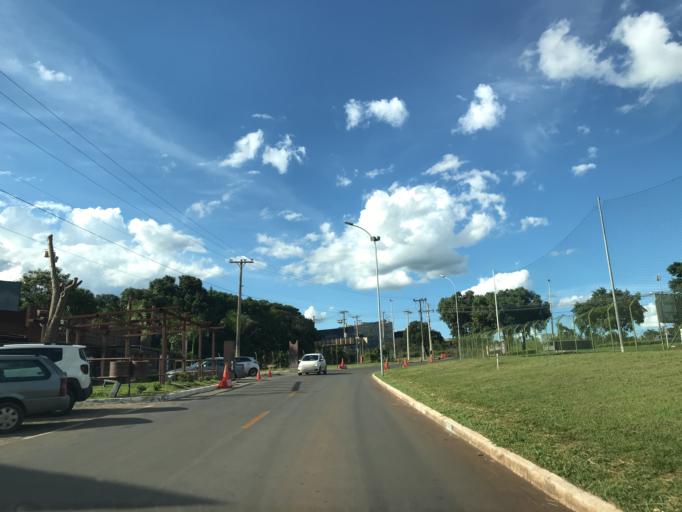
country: BR
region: Federal District
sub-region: Brasilia
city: Brasilia
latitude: -15.8178
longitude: -47.8672
